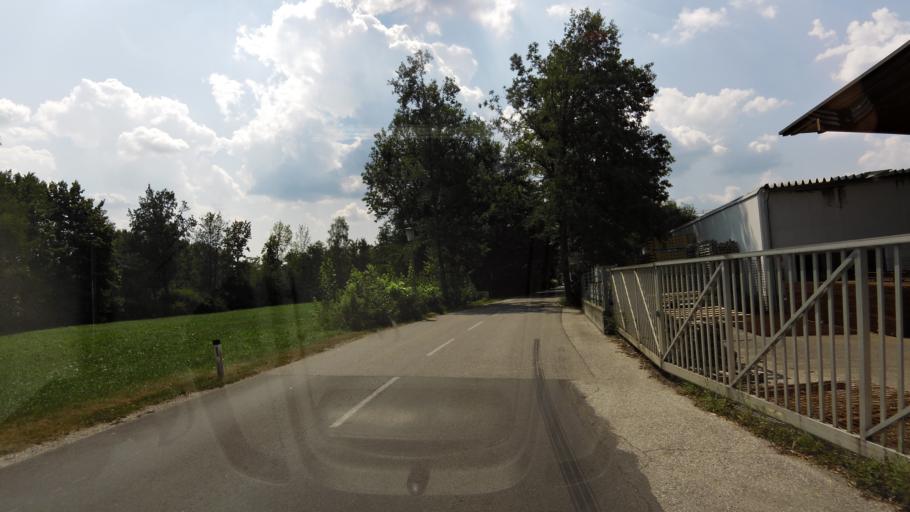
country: AT
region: Upper Austria
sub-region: Politischer Bezirk Ried im Innkreis
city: Waldzell
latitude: 48.1394
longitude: 13.4254
